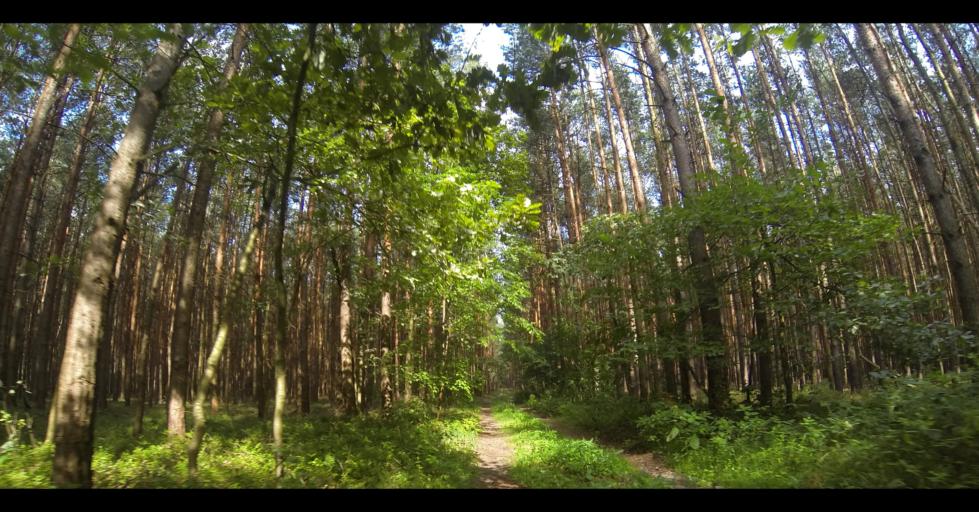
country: DE
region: Saxony
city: Thiendorf
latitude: 51.2715
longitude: 13.7348
